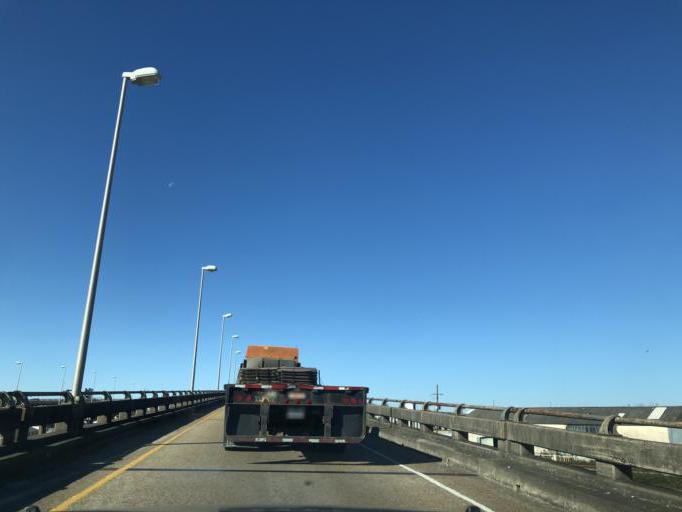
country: US
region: Louisiana
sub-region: Jefferson Parish
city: Jefferson
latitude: 29.9746
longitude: -90.1535
